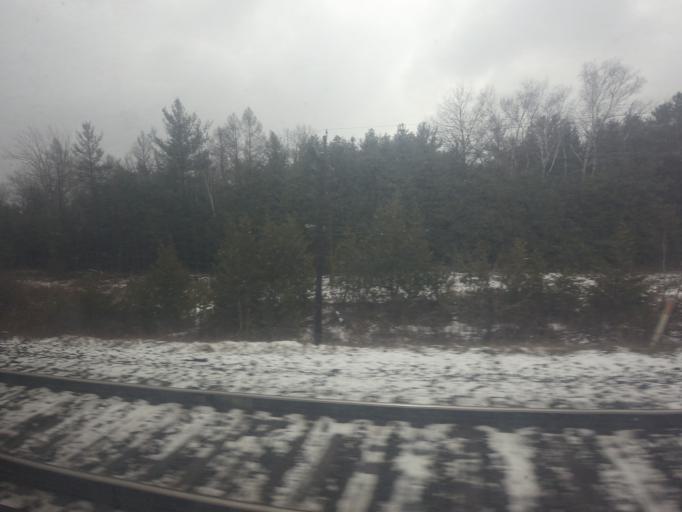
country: CA
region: Ontario
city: Quinte West
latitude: 44.0251
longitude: -77.7797
